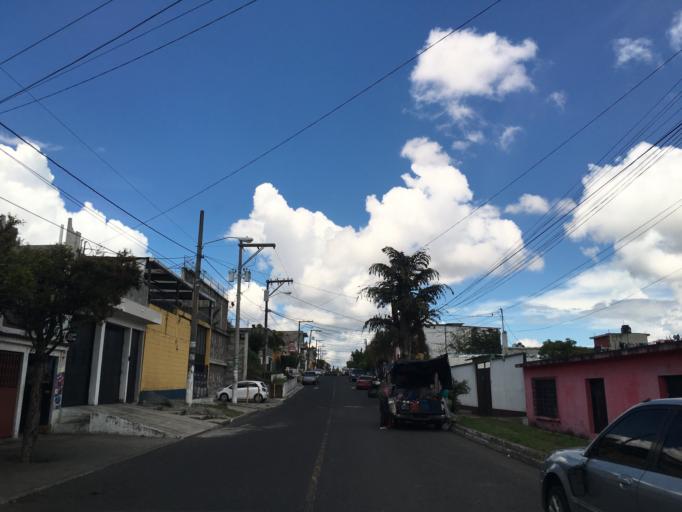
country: GT
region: Guatemala
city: Mixco
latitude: 14.6288
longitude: -90.5836
